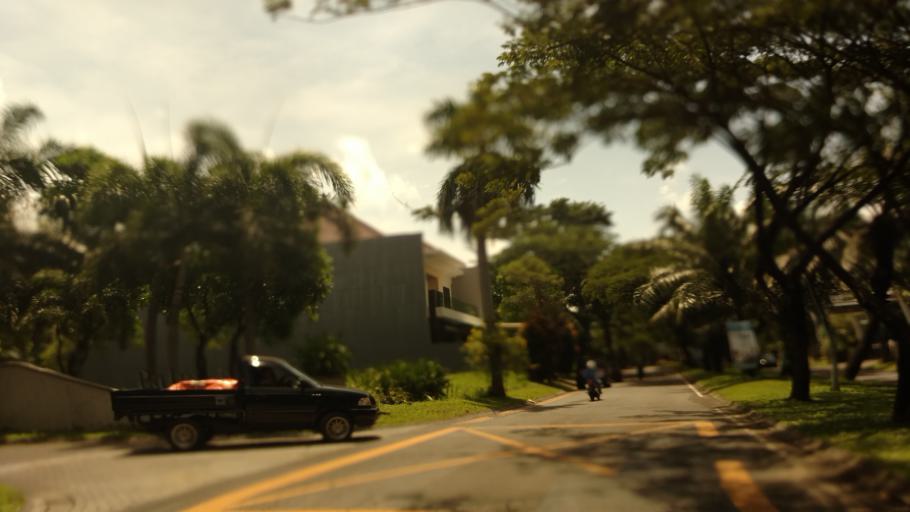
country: ID
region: East Java
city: Driyorejo
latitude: -7.2943
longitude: 112.6532
